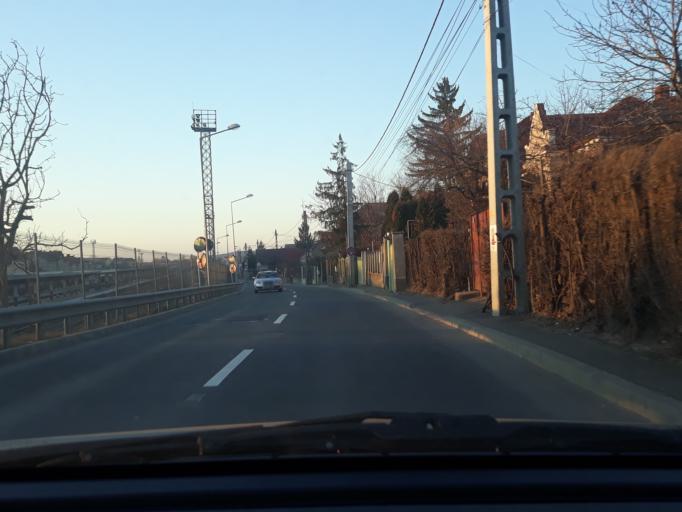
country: RO
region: Bihor
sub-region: Comuna Biharea
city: Oradea
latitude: 47.0686
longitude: 21.9378
